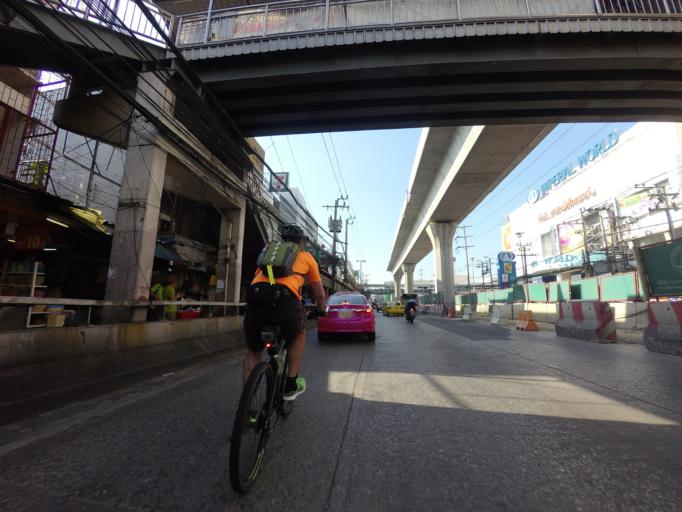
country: TH
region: Bangkok
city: Bang Na
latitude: 13.6501
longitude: 100.5978
